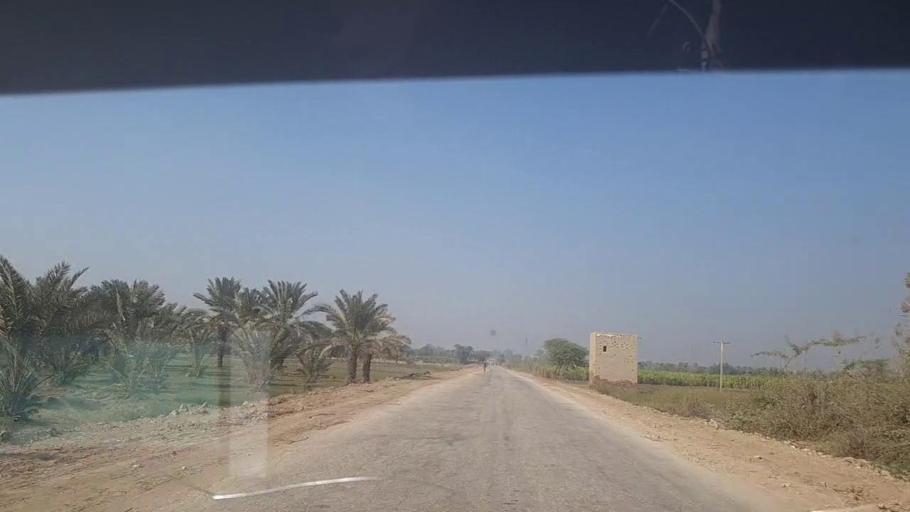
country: PK
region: Sindh
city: Kot Diji
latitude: 27.4240
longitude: 68.6580
